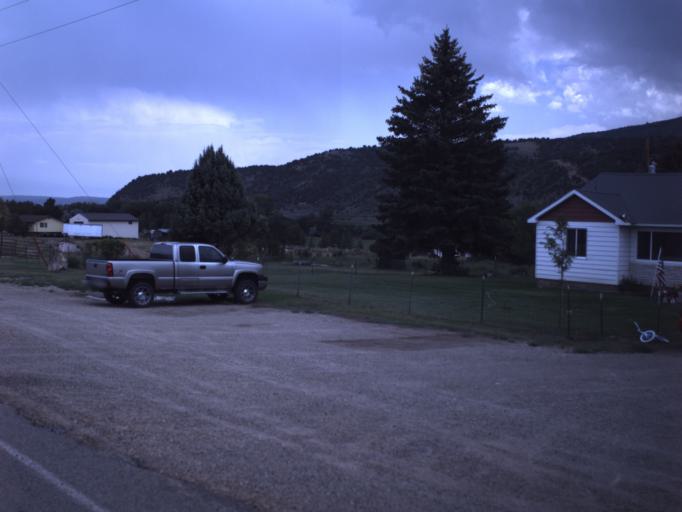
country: US
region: Utah
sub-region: Duchesne County
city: Duchesne
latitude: 40.4037
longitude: -110.7648
